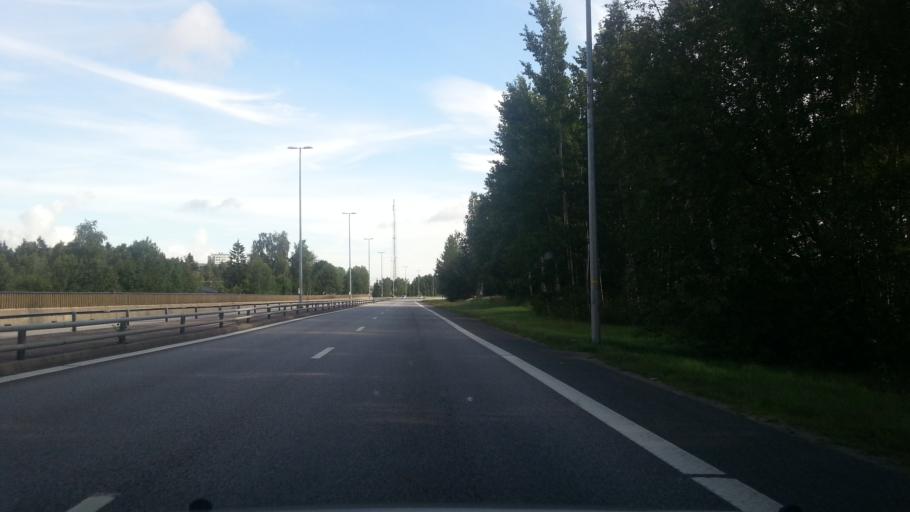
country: SE
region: Vaestra Goetaland
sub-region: Trollhattan
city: Trollhattan
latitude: 58.2739
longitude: 12.2989
